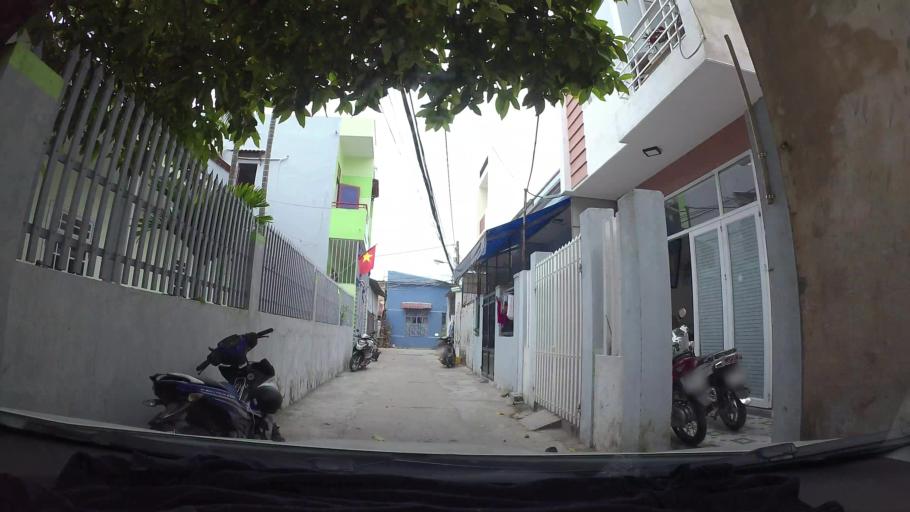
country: VN
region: Da Nang
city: Lien Chieu
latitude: 16.0637
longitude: 108.1653
